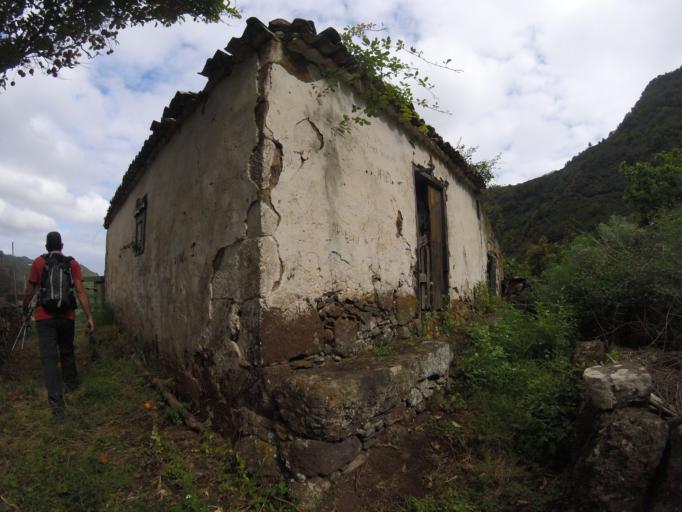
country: ES
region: Canary Islands
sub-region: Provincia de Santa Cruz de Tenerife
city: Tegueste
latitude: 28.5482
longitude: -16.2834
